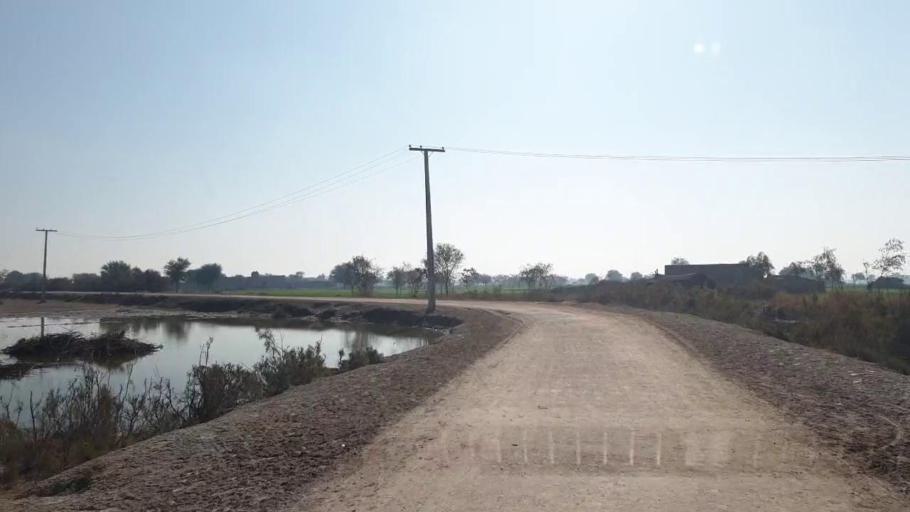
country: PK
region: Sindh
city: Nawabshah
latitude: 26.0822
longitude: 68.4769
